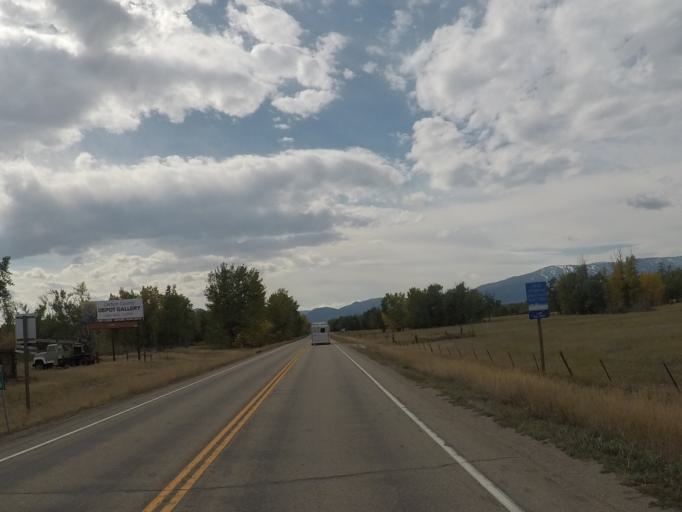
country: US
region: Montana
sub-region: Carbon County
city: Red Lodge
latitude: 45.2762
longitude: -109.2180
